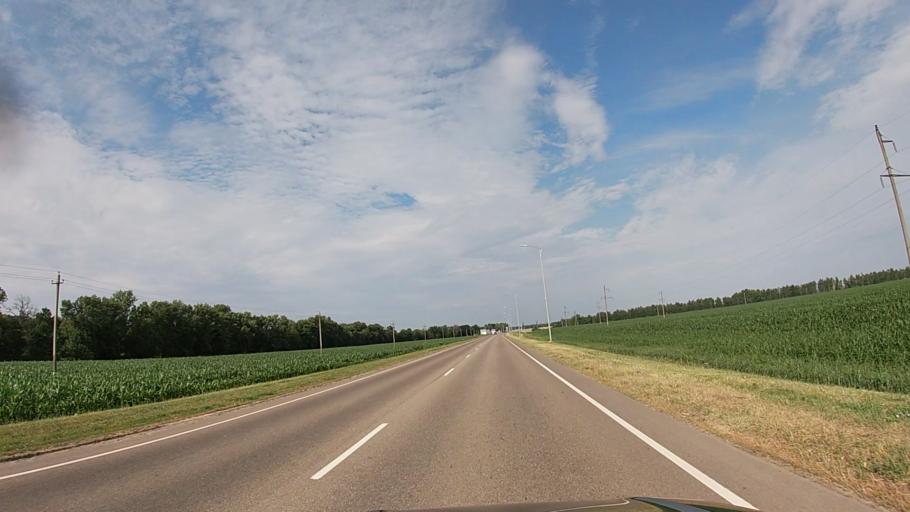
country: RU
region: Belgorod
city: Proletarskiy
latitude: 50.7992
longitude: 35.7248
